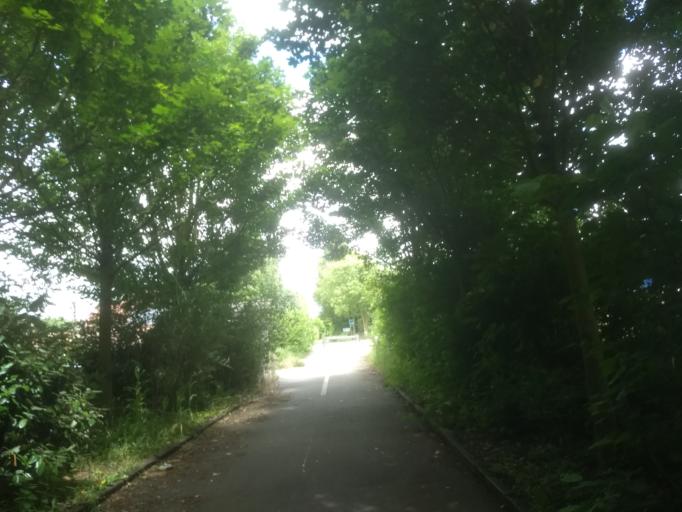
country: FR
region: Nord-Pas-de-Calais
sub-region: Departement du Pas-de-Calais
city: Beaumetz-les-Loges
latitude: 50.2393
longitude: 2.6613
